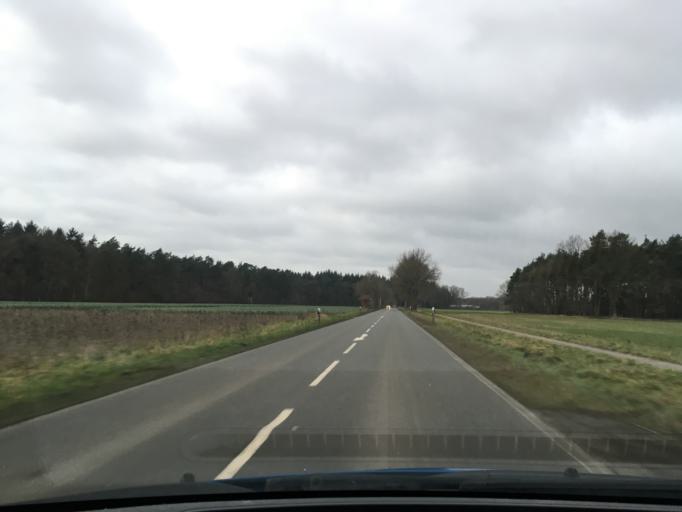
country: DE
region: Lower Saxony
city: Vogelsen
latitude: 53.2958
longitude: 10.3511
